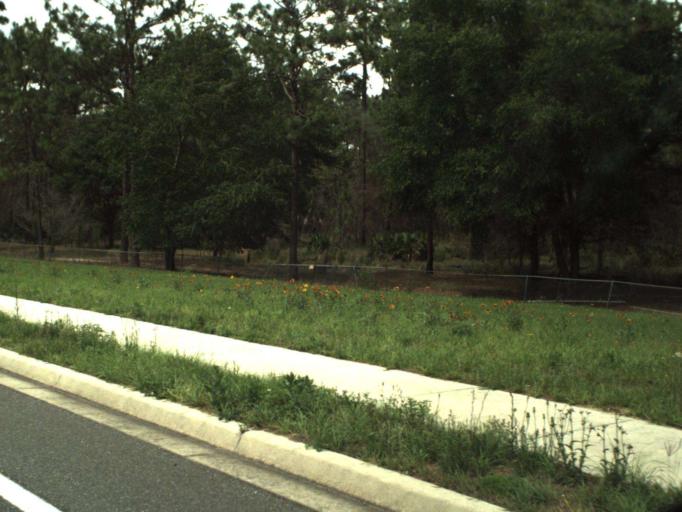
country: US
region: Florida
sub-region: Marion County
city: Ocala
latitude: 29.2057
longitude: -82.0542
